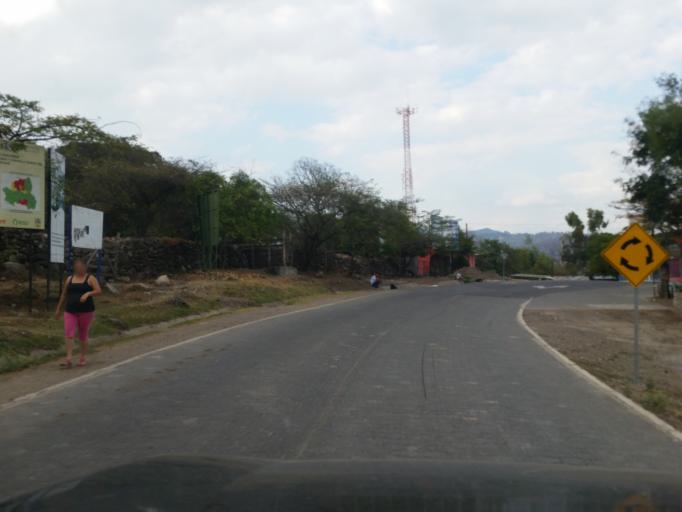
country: NI
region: Jinotega
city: La Concordia
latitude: 13.1940
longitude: -86.1682
